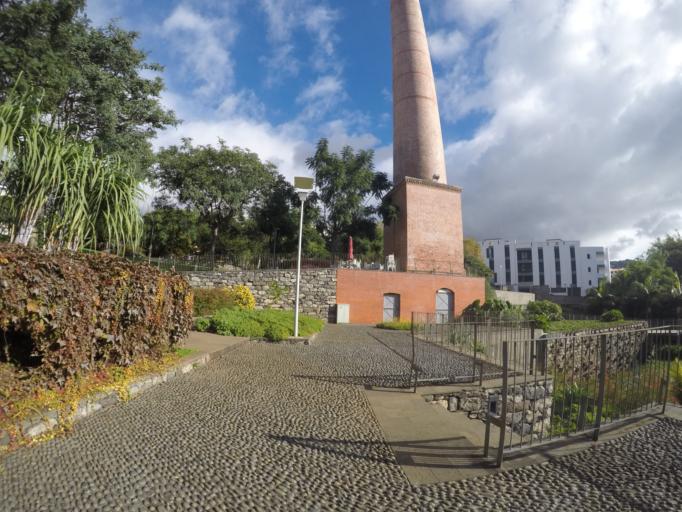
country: PT
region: Madeira
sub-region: Funchal
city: Nossa Senhora do Monte
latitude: 32.6537
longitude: -16.9117
